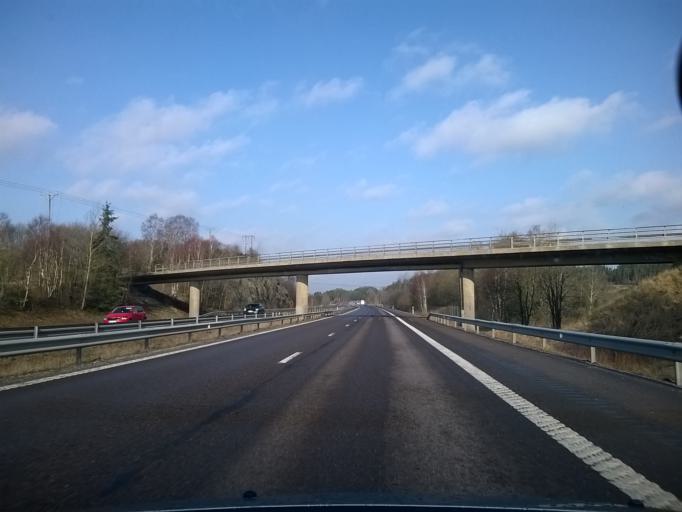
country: SE
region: Vaestra Goetaland
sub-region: Kungalvs Kommun
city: Kode
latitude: 57.9035
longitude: 11.9125
